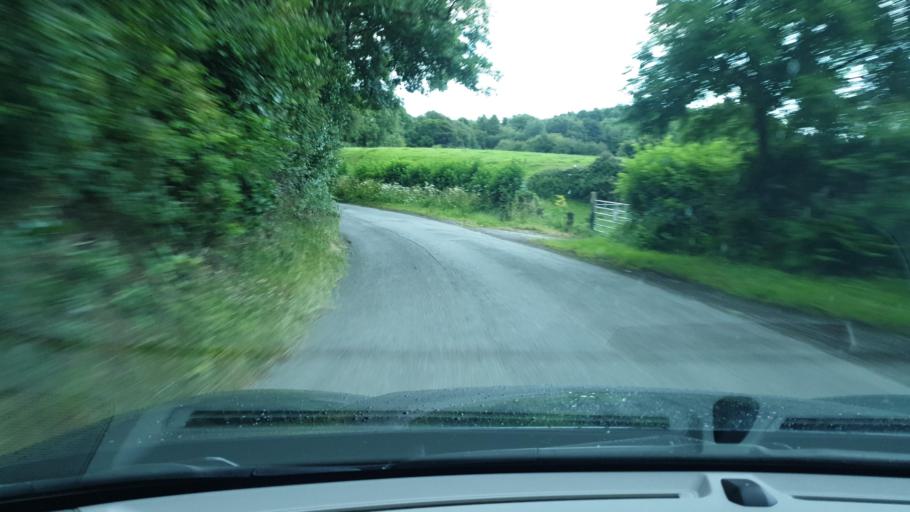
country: IE
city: Kentstown
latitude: 53.6020
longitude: -6.6024
